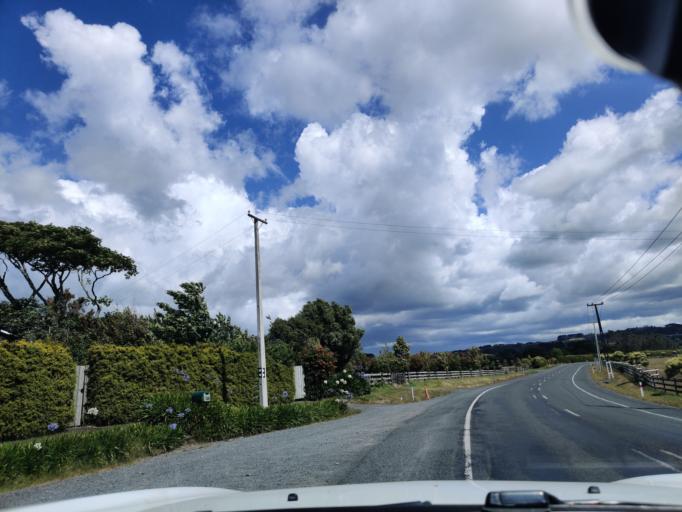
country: NZ
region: Auckland
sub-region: Auckland
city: Red Hill
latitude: -37.0152
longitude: 175.0252
